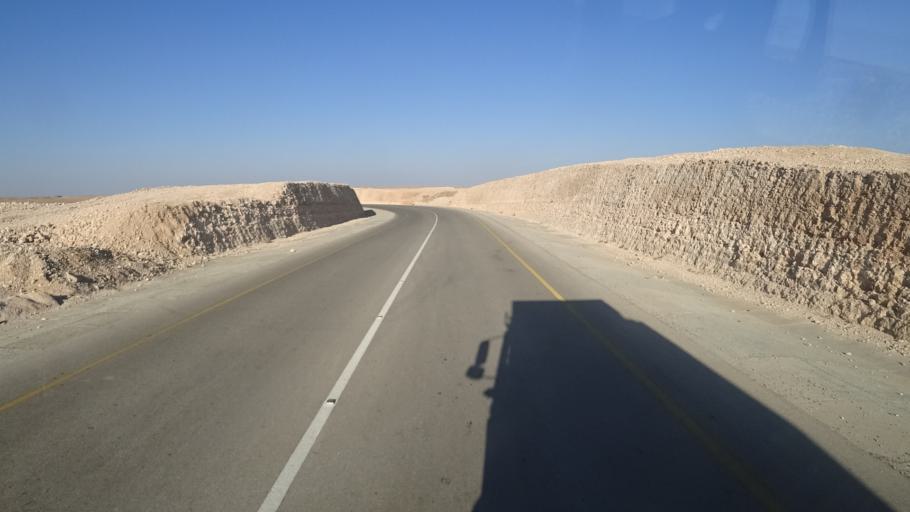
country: YE
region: Al Mahrah
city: Hawf
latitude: 17.0885
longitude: 53.0355
